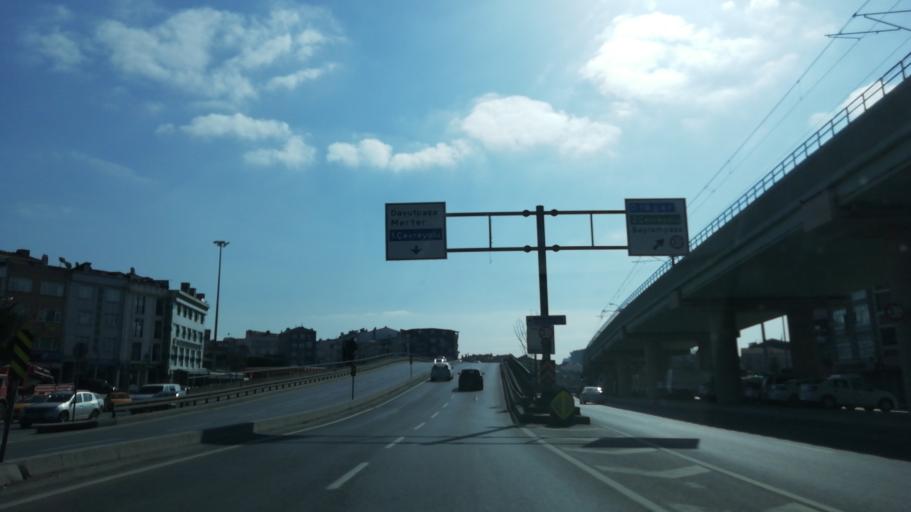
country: TR
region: Istanbul
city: Esenler
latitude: 41.0350
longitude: 28.8953
